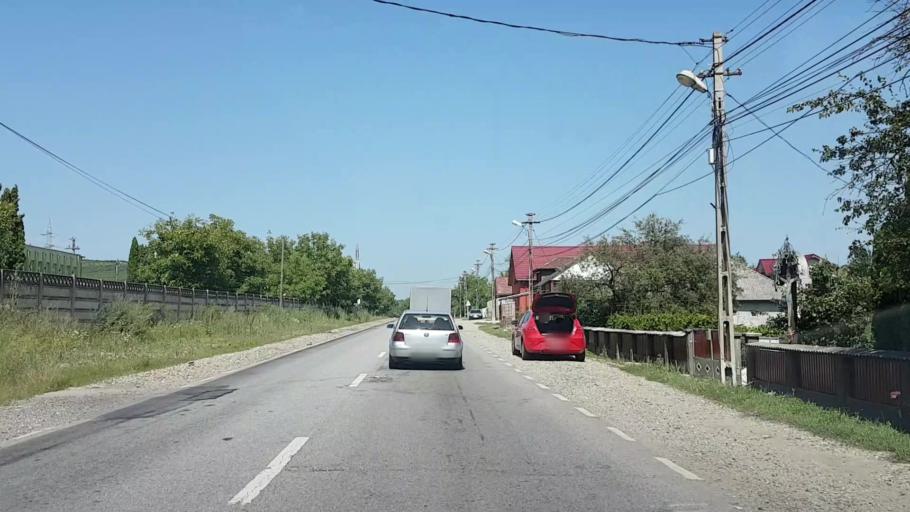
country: RO
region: Cluj
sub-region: Comuna Cusdrioara
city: Cusdrioara
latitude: 47.1637
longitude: 23.8970
